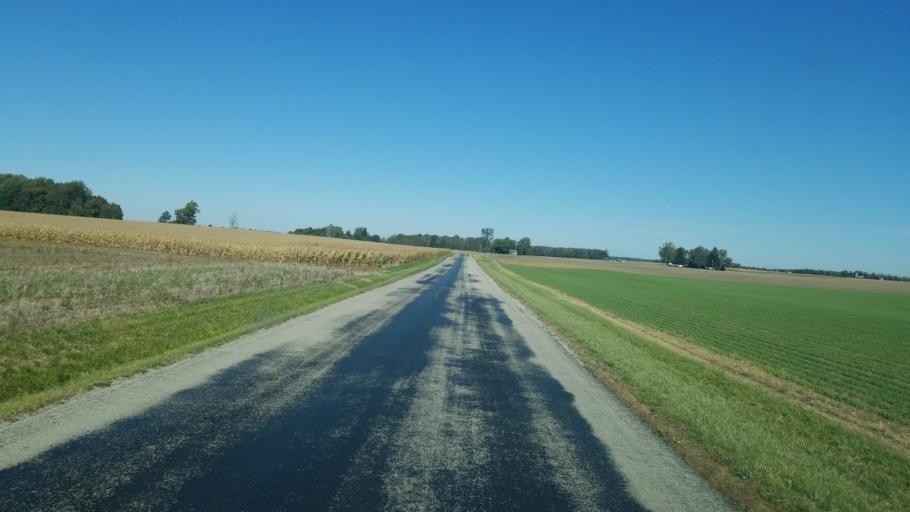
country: US
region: Ohio
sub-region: Richland County
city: Shelby
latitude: 40.8830
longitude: -82.6959
